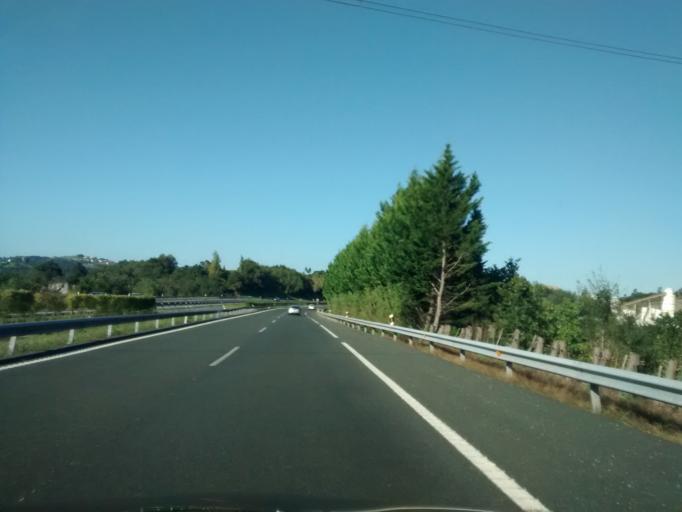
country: ES
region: Cantabria
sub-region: Provincia de Cantabria
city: Luzmela
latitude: 43.3327
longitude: -4.1591
